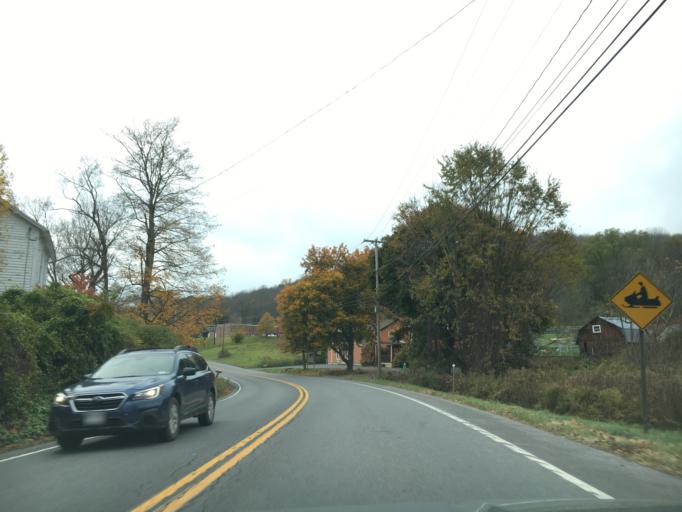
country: US
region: New York
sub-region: Otsego County
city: Cooperstown
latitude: 42.6554
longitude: -74.9637
